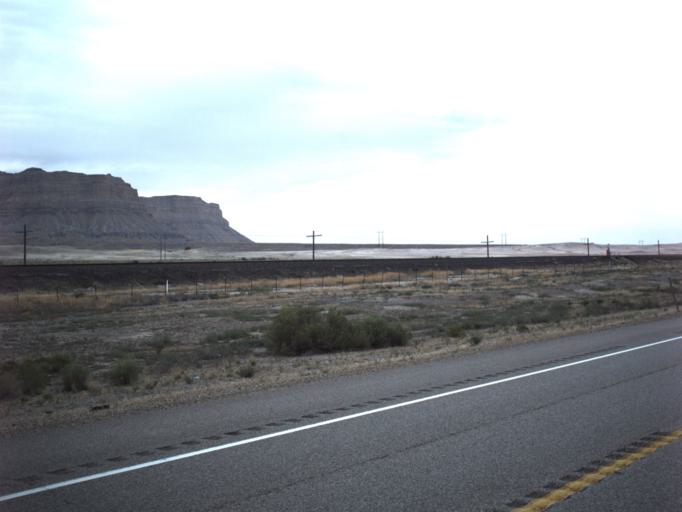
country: US
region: Utah
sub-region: Carbon County
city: East Carbon City
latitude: 39.1037
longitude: -110.3247
